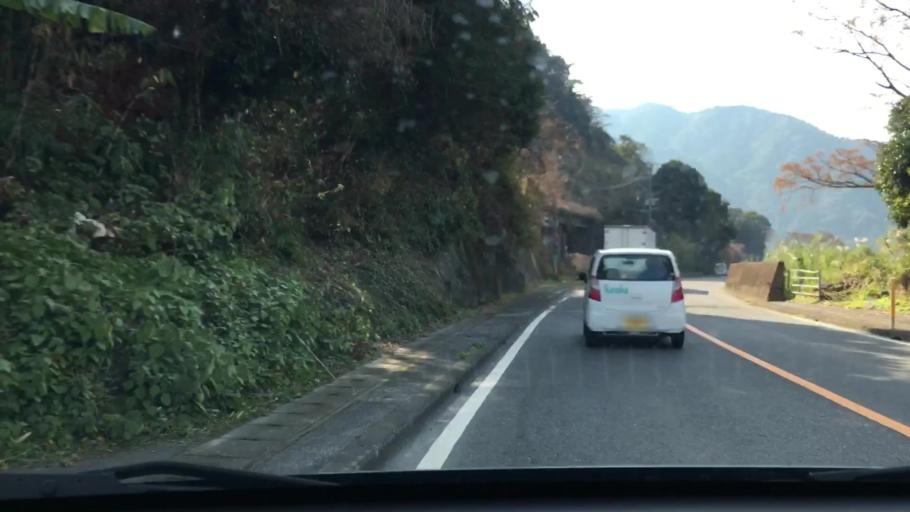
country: JP
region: Kagoshima
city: Hamanoichi
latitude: 31.5899
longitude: 130.7880
